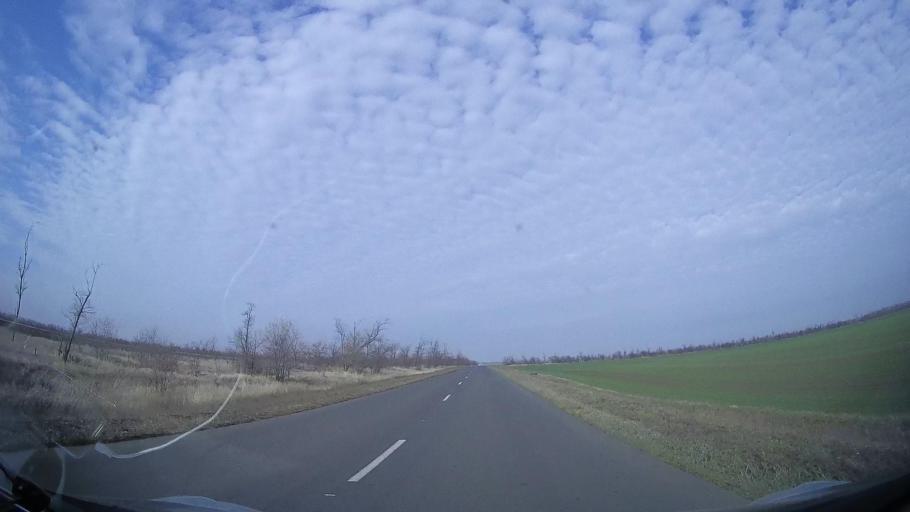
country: RU
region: Rostov
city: Gigant
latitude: 46.8565
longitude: 41.2818
